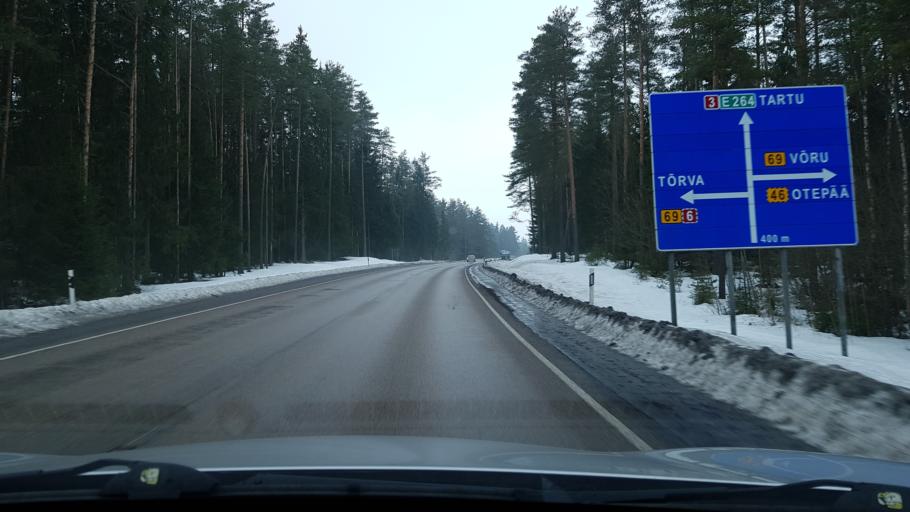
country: EE
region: Valgamaa
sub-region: Torva linn
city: Torva
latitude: 58.0059
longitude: 26.1625
